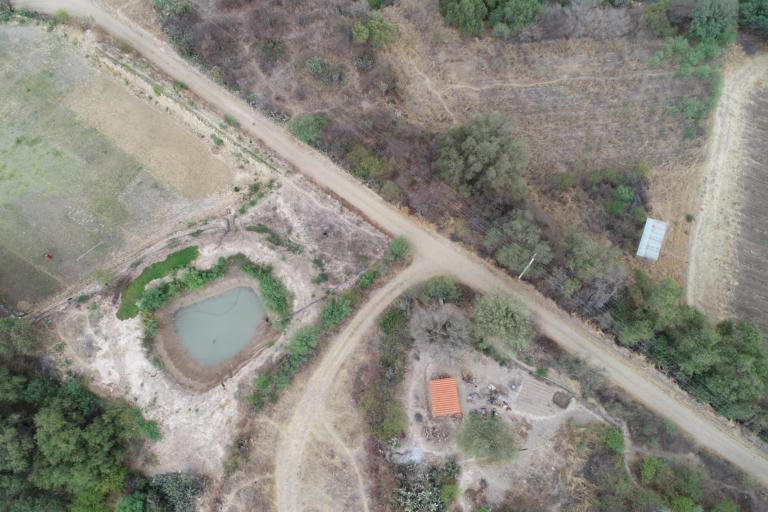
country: BO
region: Tarija
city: Tarija
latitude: -21.6014
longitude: -64.6189
